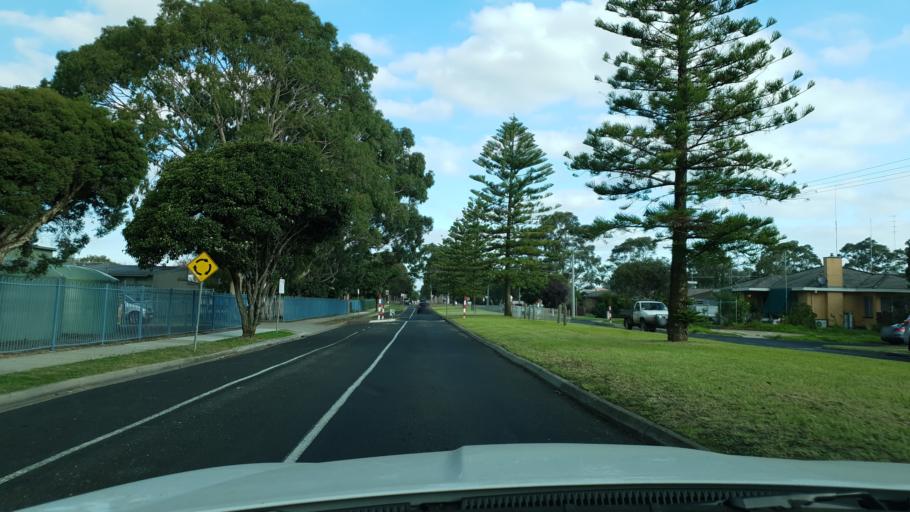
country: AU
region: Victoria
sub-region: East Gippsland
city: Bairnsdale
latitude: -37.8230
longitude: 147.6078
